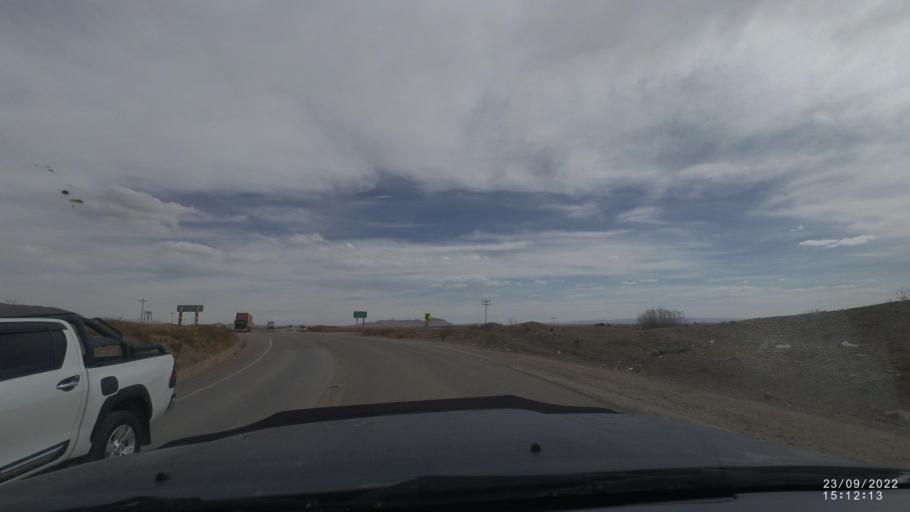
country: BO
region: Oruro
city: Oruro
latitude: -17.8217
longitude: -67.0281
